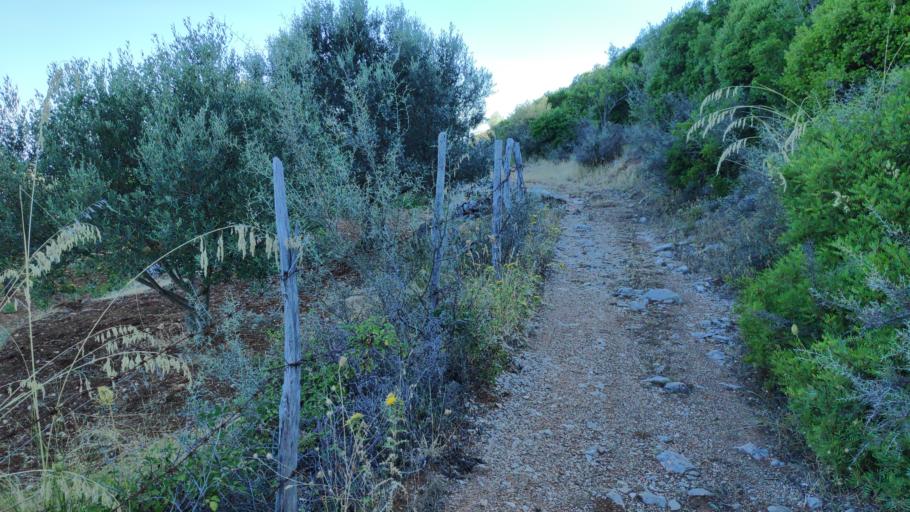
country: IT
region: Calabria
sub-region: Provincia di Reggio Calabria
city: Pazzano
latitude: 38.4587
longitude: 16.4370
